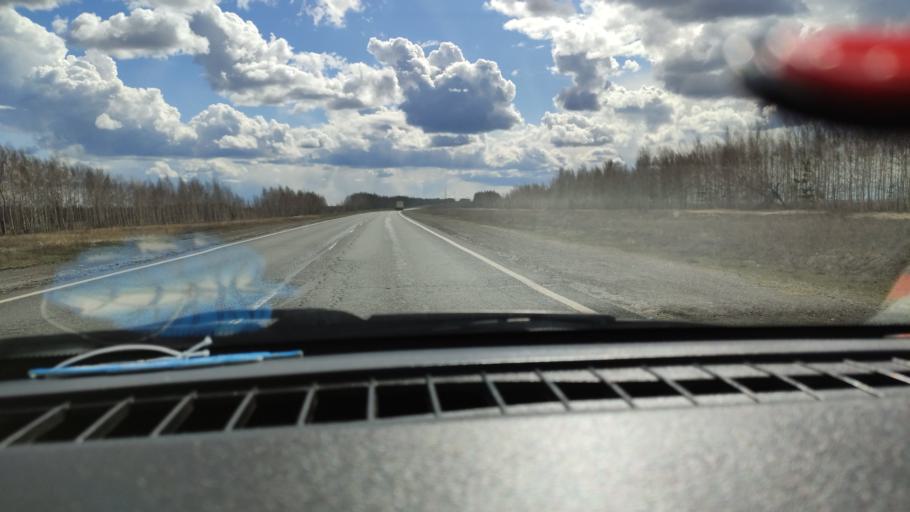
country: RU
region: Saratov
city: Dukhovnitskoye
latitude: 52.8479
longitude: 48.2543
